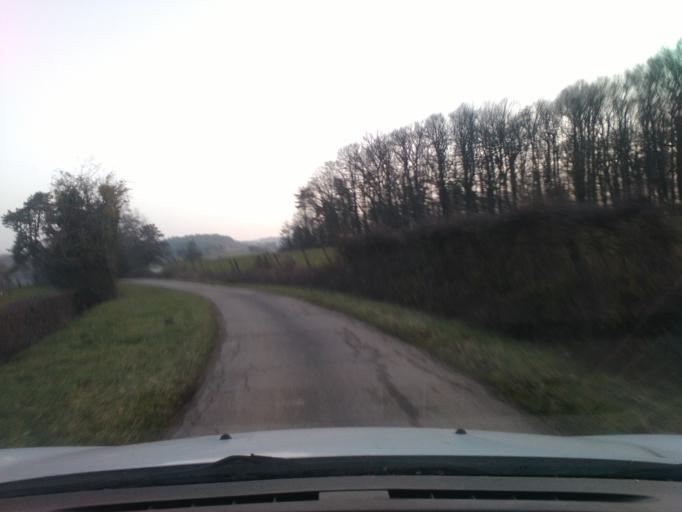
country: FR
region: Lorraine
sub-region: Departement des Vosges
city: Vittel
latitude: 48.2583
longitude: 5.9995
